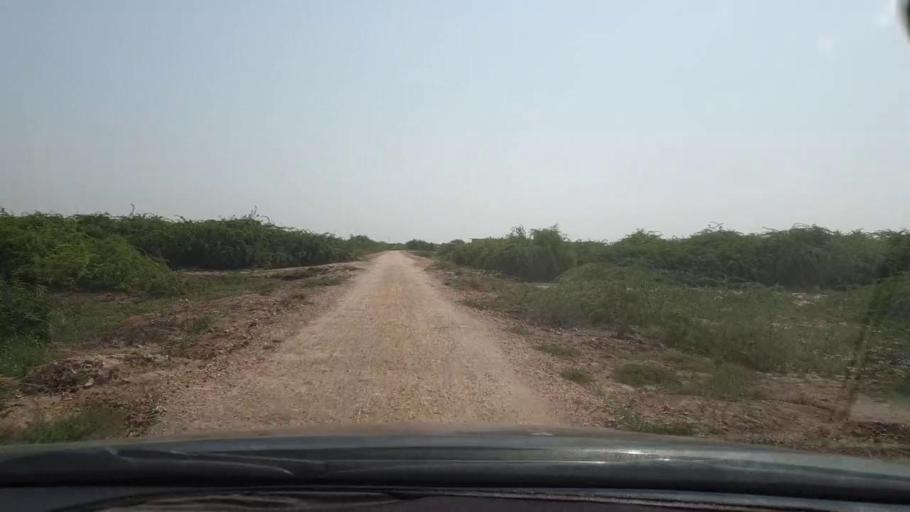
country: PK
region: Sindh
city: Naukot
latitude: 24.8079
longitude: 69.2441
